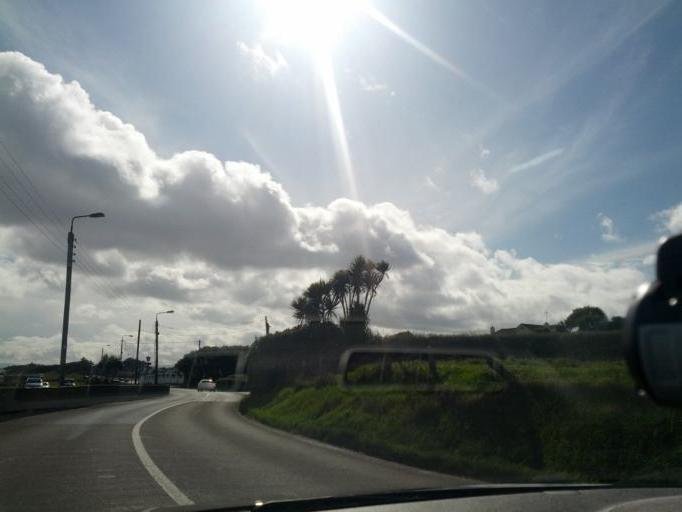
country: IE
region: Leinster
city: Portmarnock
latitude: 53.4368
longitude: -6.1221
